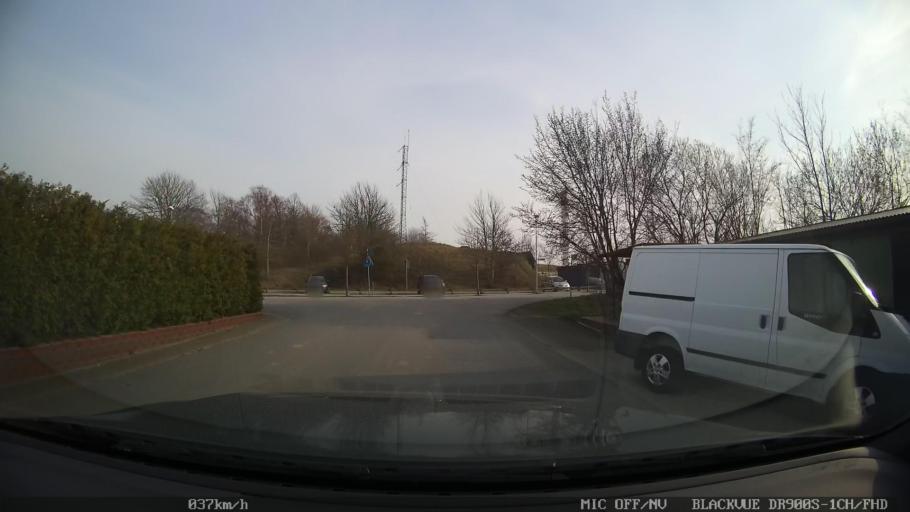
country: SE
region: Skane
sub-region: Ystads Kommun
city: Ystad
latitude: 55.4505
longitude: 13.7960
